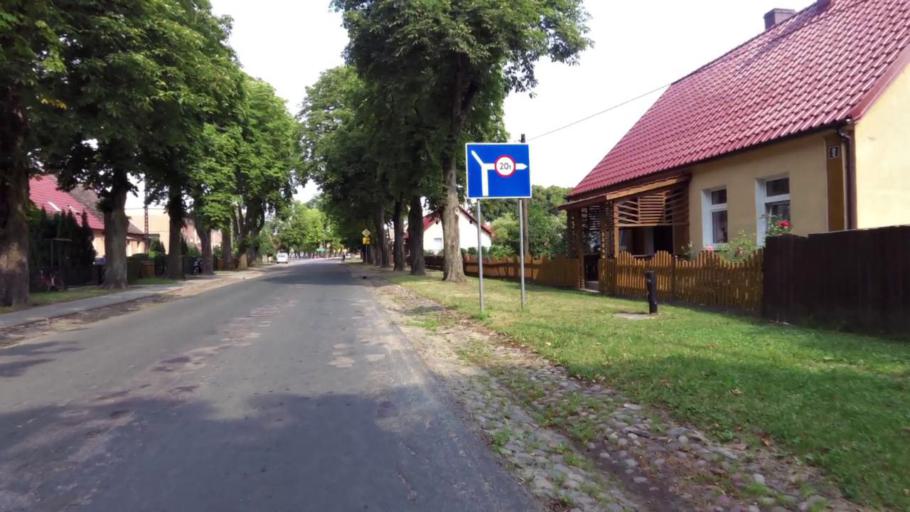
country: PL
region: West Pomeranian Voivodeship
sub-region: Powiat mysliborski
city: Debno
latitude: 52.8515
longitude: 14.6724
